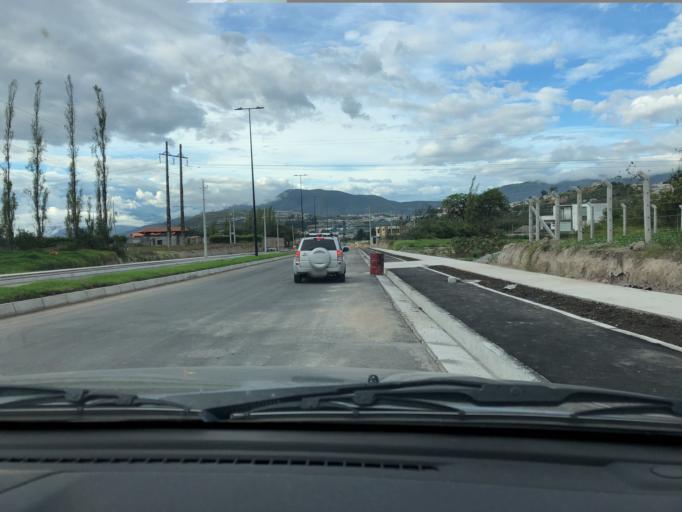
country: EC
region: Imbabura
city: Ibarra
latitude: 0.3405
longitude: -78.1545
